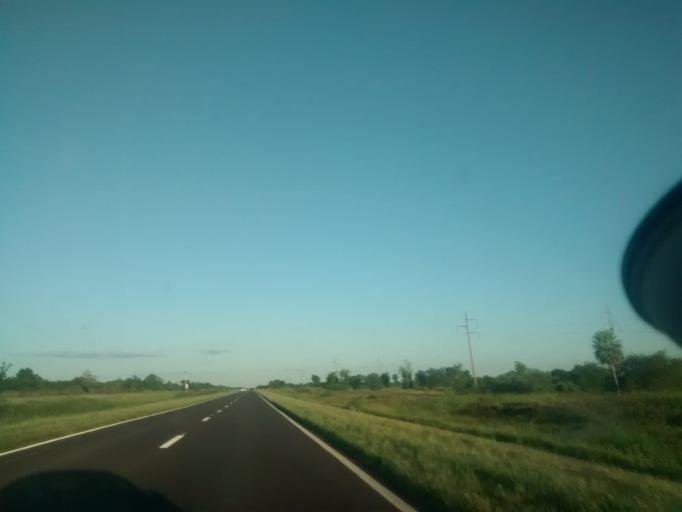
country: AR
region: Chaco
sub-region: Departamento de Presidencia de la Plaza
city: Presidencia de la Plaza
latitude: -27.0256
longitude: -59.7972
